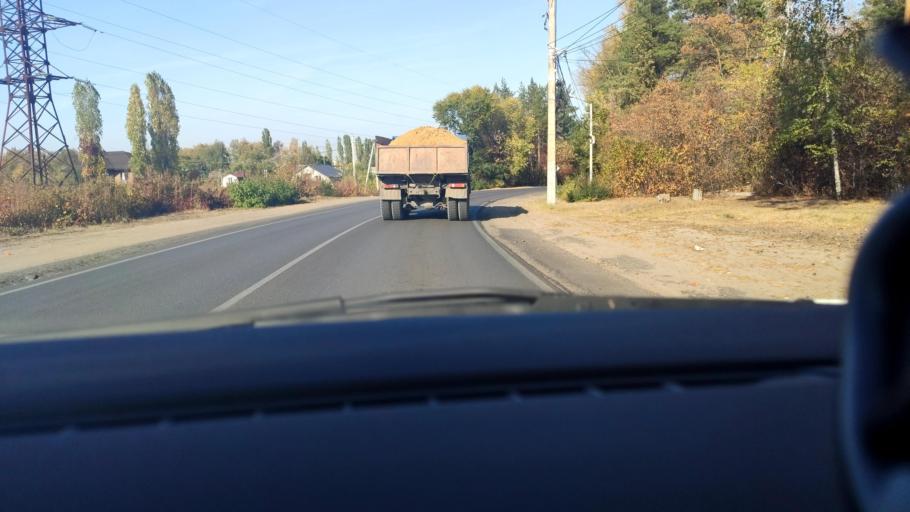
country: RU
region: Voronezj
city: Pridonskoy
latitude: 51.6330
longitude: 39.0825
